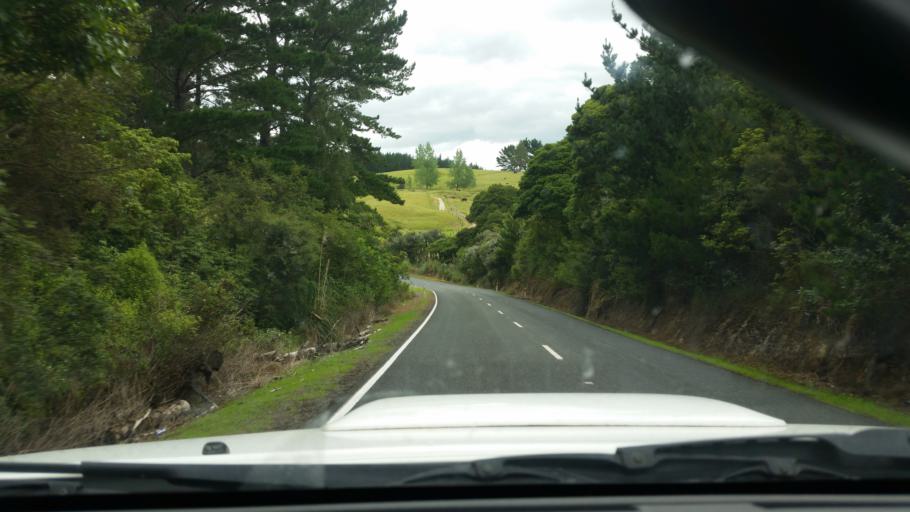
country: NZ
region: Northland
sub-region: Kaipara District
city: Dargaville
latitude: -35.7354
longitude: 173.8648
